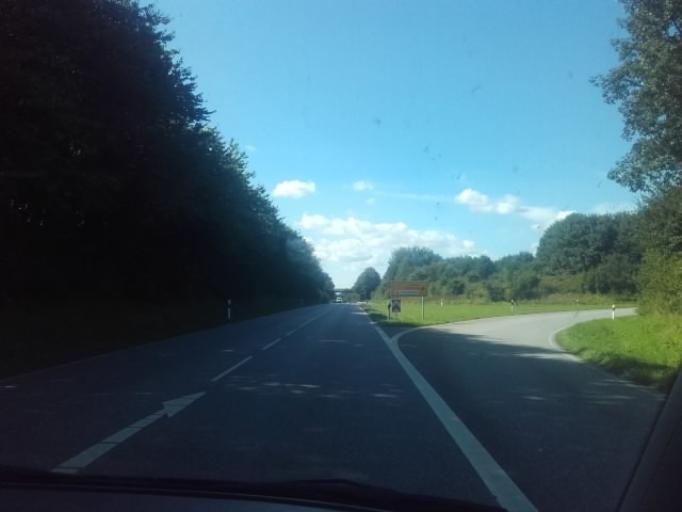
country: DE
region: Schleswig-Holstein
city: Neuberend
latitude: 54.5320
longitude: 9.5301
